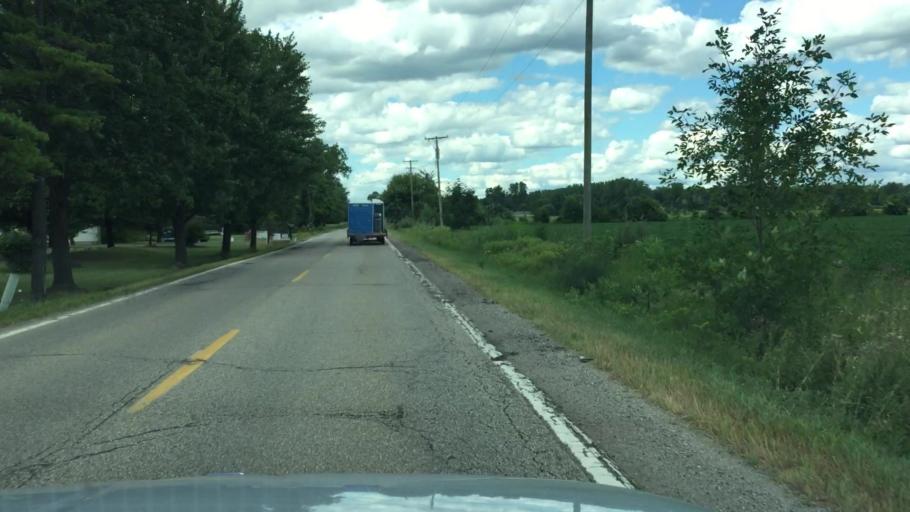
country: US
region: Michigan
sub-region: Macomb County
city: Armada
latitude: 42.8581
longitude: -82.9446
